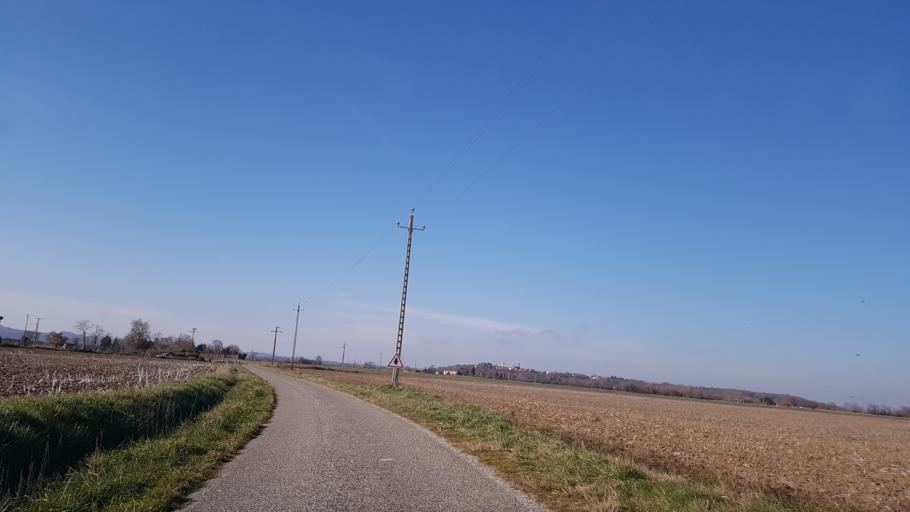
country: FR
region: Midi-Pyrenees
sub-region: Departement de l'Ariege
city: La Tour-du-Crieu
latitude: 43.1728
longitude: 1.6626
